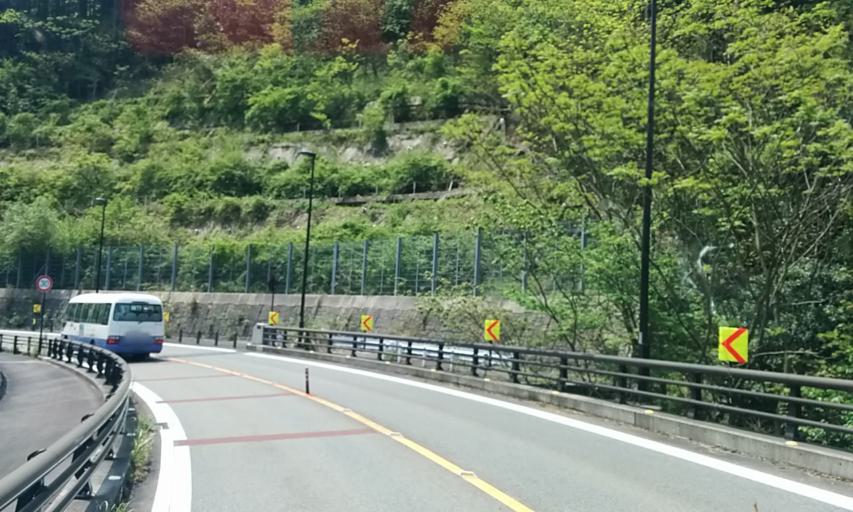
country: JP
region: Ehime
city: Niihama
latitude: 33.8957
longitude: 133.3092
